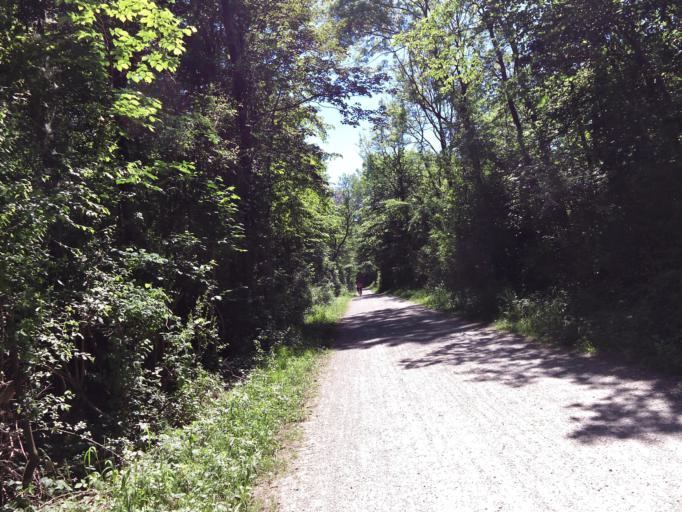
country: DE
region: Bavaria
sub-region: Upper Bavaria
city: Unterfoehring
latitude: 48.2001
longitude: 11.6347
